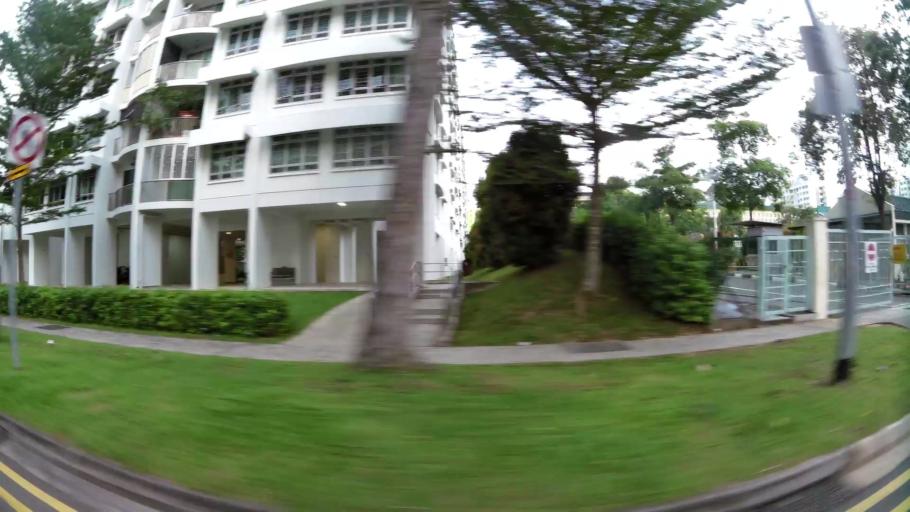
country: MY
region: Johor
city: Kampung Pasir Gudang Baru
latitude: 1.4219
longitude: 103.8438
